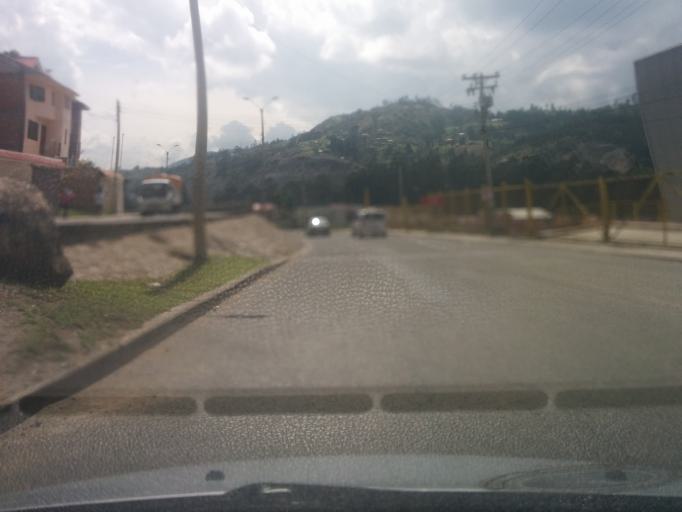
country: EC
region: Azuay
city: Cuenca
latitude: -2.8900
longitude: -78.9632
